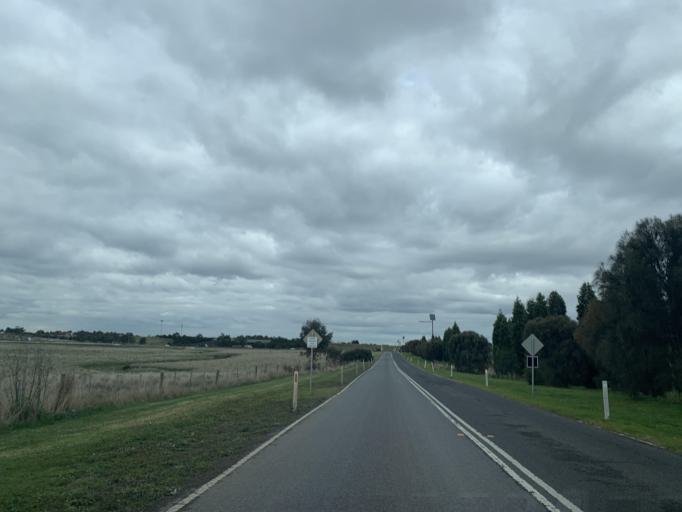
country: AU
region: Victoria
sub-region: Hume
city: Craigieburn
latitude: -37.5981
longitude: 144.9735
